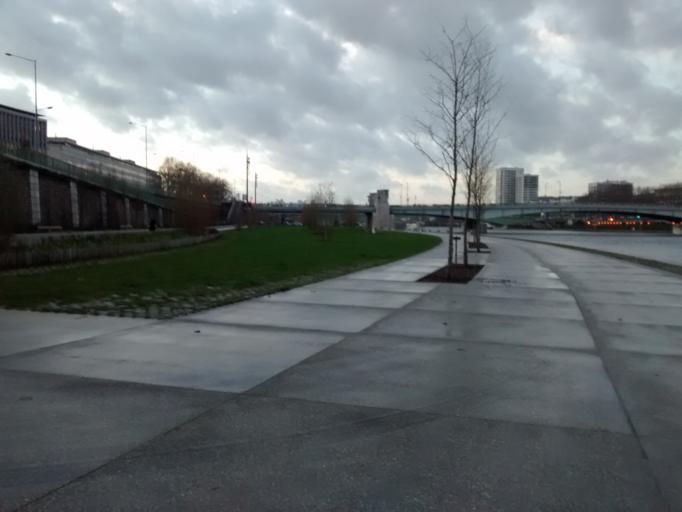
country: FR
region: Haute-Normandie
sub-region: Departement de la Seine-Maritime
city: Rouen
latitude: 49.4354
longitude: 1.0936
